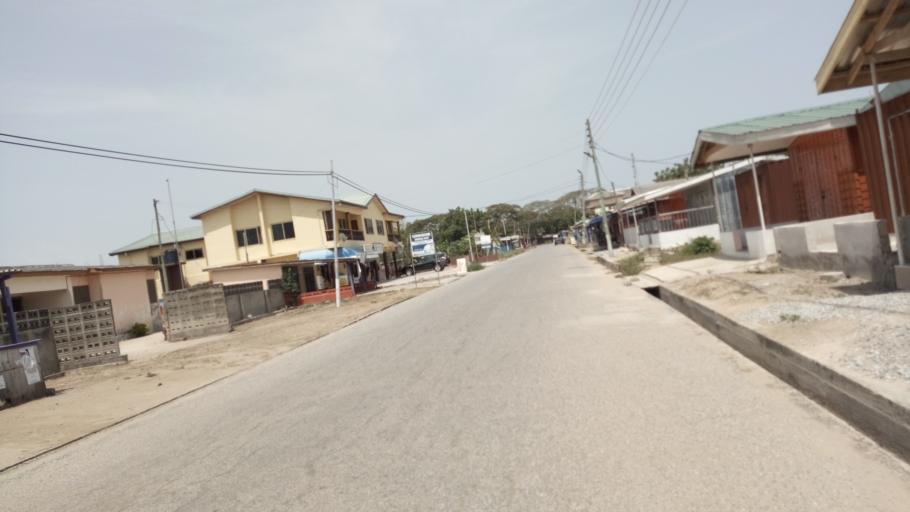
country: GH
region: Central
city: Winneba
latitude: 5.3575
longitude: -0.6342
